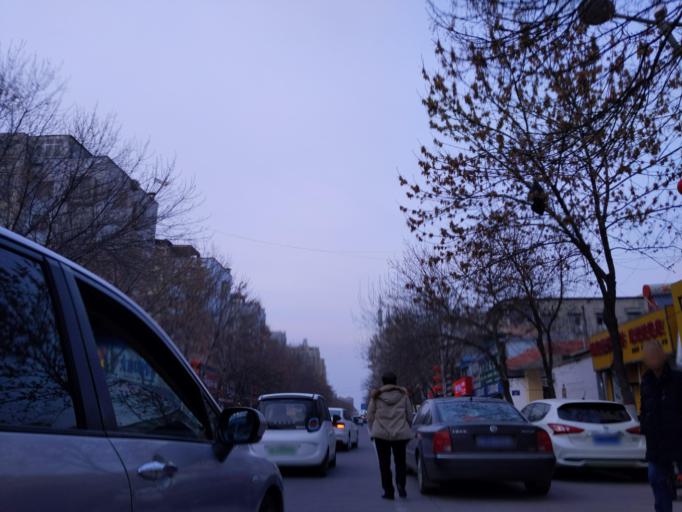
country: CN
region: Henan Sheng
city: Zhongyuanlu
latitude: 35.7826
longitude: 115.0390
